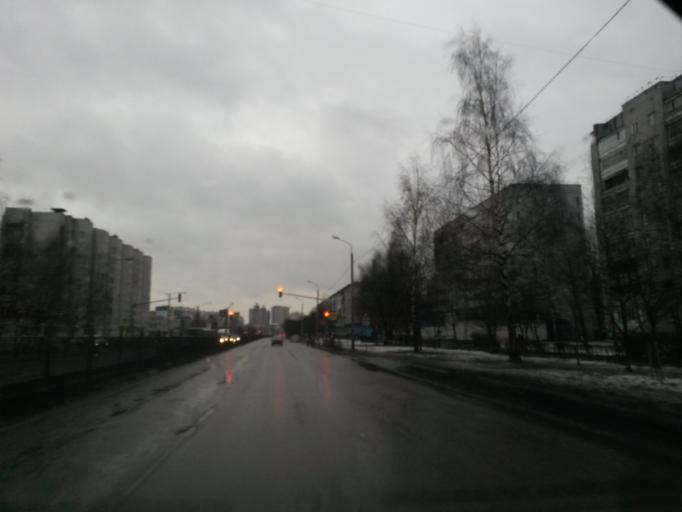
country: RU
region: Jaroslavl
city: Yaroslavl
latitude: 57.6536
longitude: 39.9439
